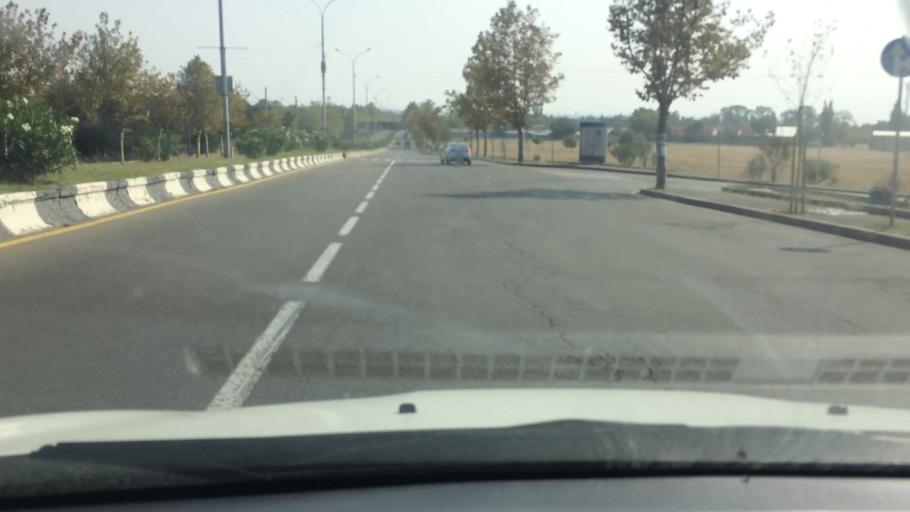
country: GE
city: Didi Lilo
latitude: 41.6835
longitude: 44.9546
